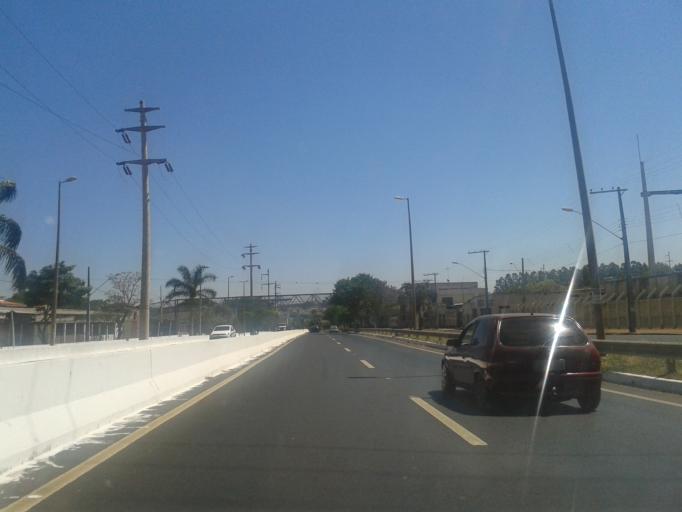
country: BR
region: Minas Gerais
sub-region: Uberlandia
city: Uberlandia
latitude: -18.9074
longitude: -48.2991
